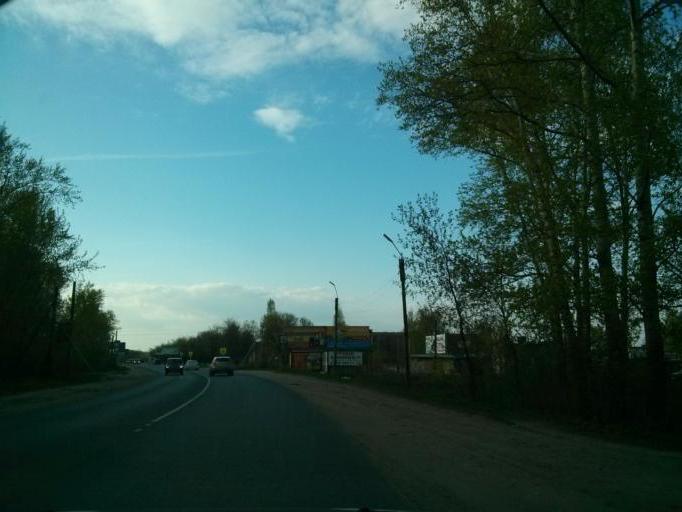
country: RU
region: Vladimir
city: Murom
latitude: 55.5968
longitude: 42.0337
